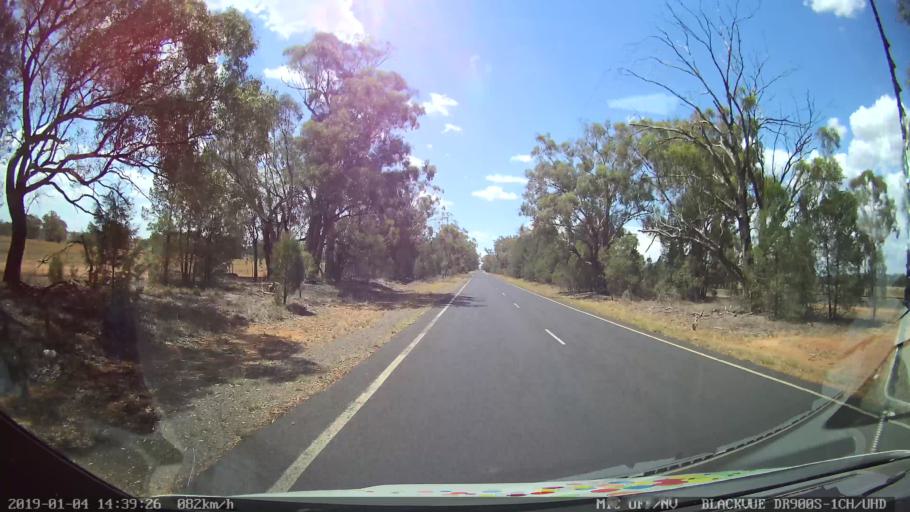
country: AU
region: New South Wales
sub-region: Dubbo Municipality
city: Dubbo
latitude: -32.1647
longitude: 148.6329
